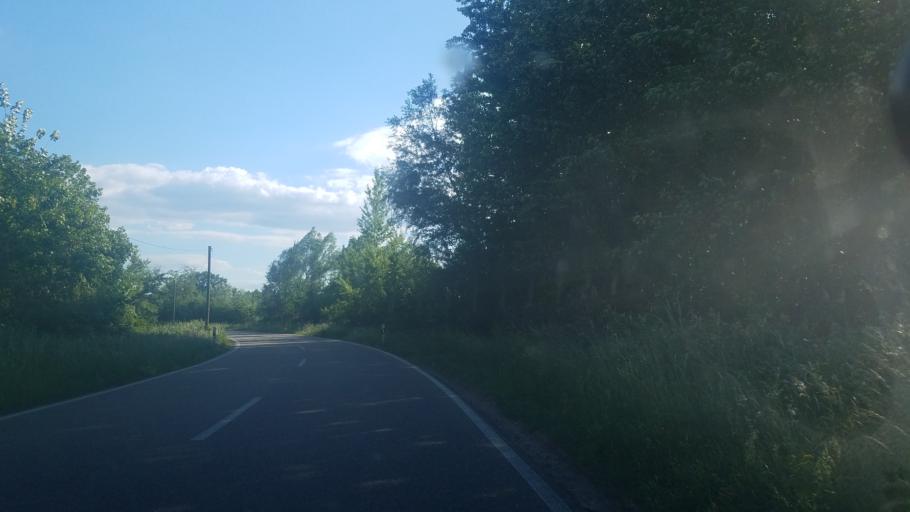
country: FR
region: Alsace
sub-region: Departement du Bas-Rhin
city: Kilstett
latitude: 48.6490
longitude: 7.8631
